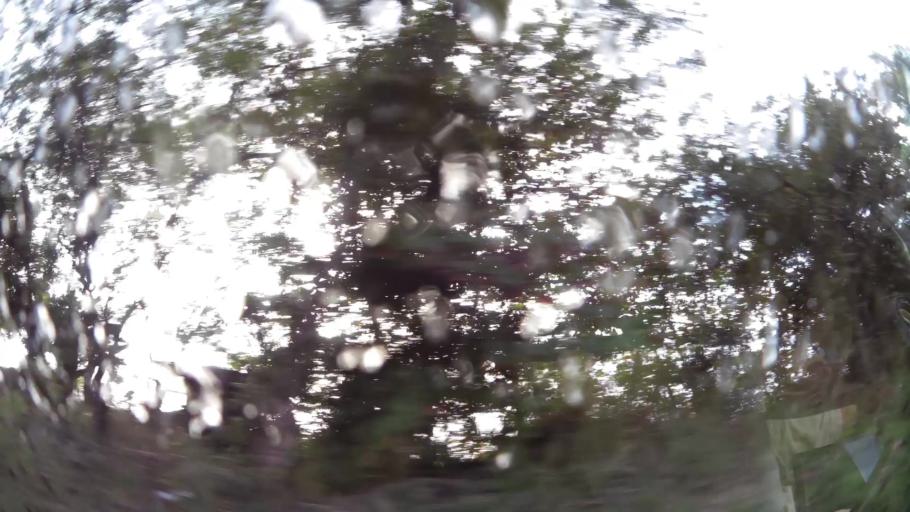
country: DM
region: Saint Paul
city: Mahaut
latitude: 15.3721
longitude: -61.4050
